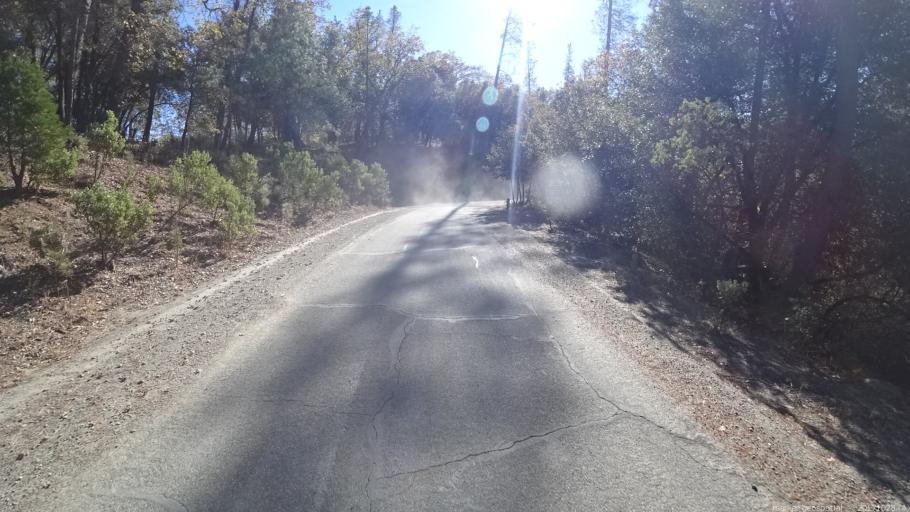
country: US
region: California
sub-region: Shasta County
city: Shasta
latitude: 40.6118
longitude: -122.5745
